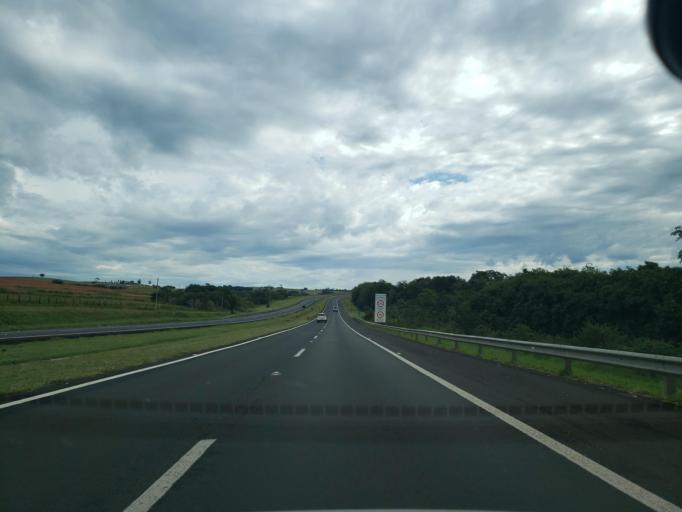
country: BR
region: Sao Paulo
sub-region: Bauru
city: Bauru
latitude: -22.1962
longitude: -49.1921
